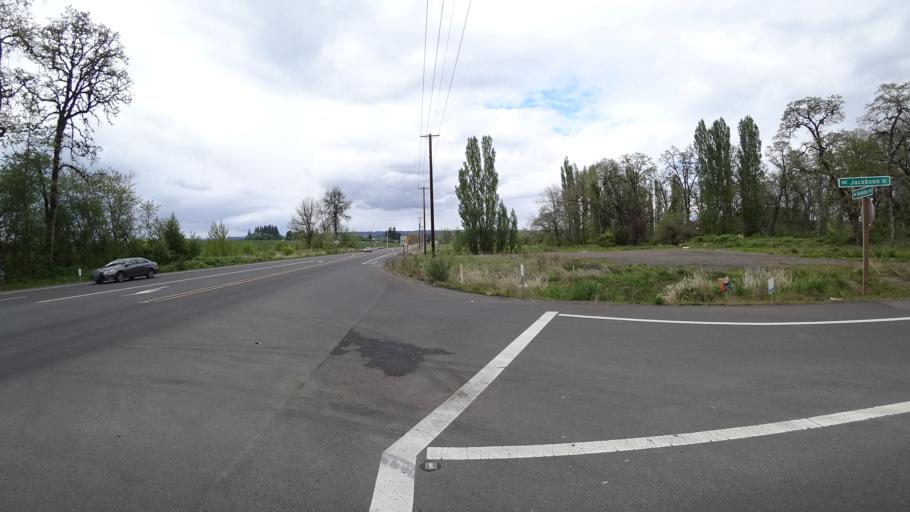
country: US
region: Oregon
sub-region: Washington County
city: Rockcreek
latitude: 45.5678
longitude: -122.9252
